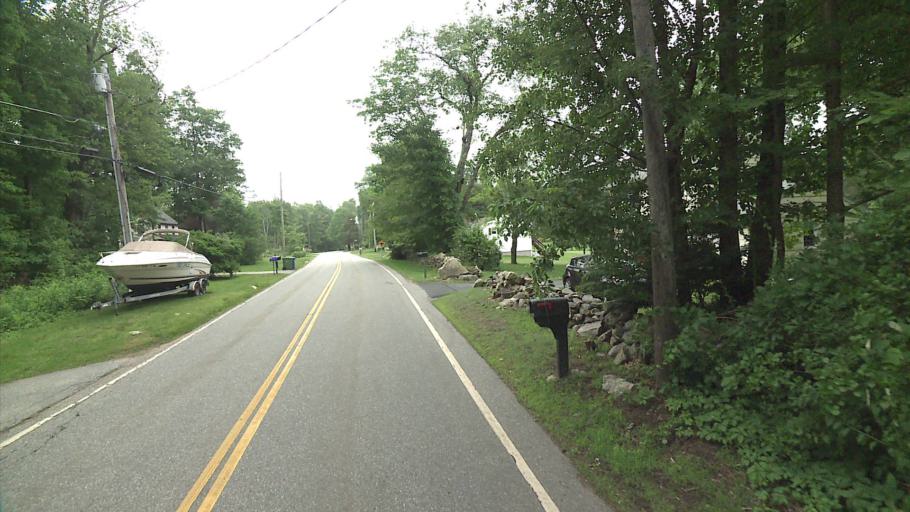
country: US
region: Connecticut
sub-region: Tolland County
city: Hebron
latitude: 41.6878
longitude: -72.3611
